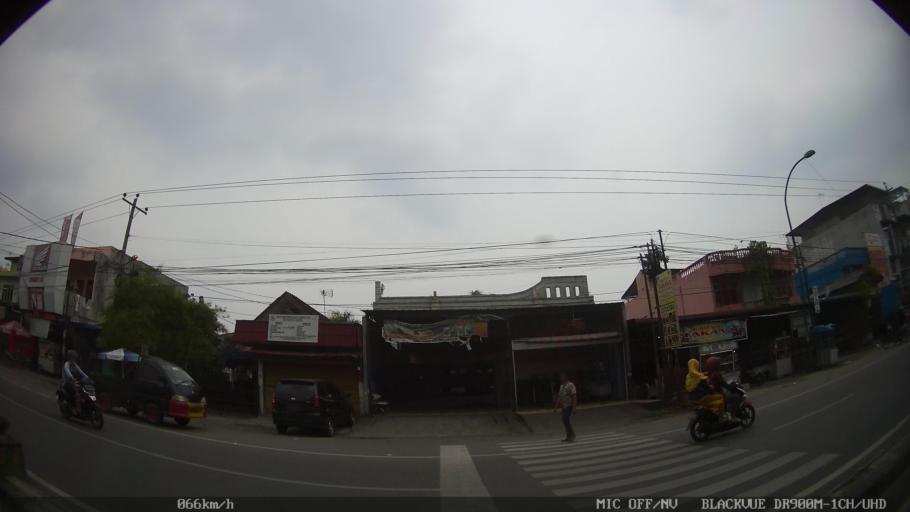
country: ID
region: North Sumatra
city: Medan
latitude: 3.5708
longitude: 98.7032
